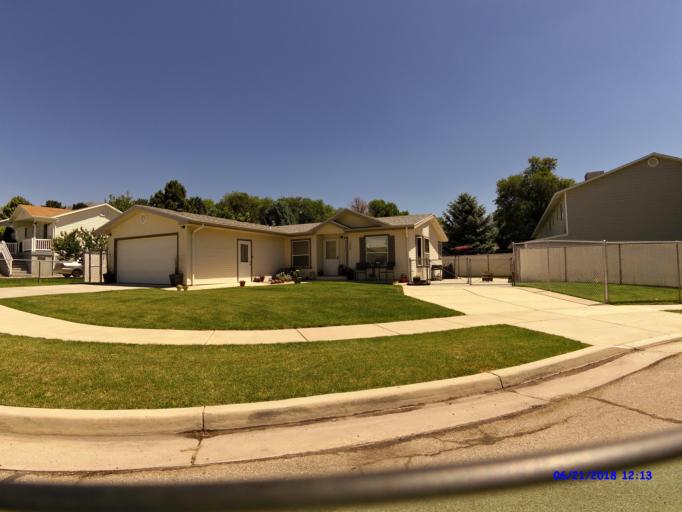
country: US
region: Utah
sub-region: Weber County
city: Harrisville
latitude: 41.2832
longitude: -112.0014
